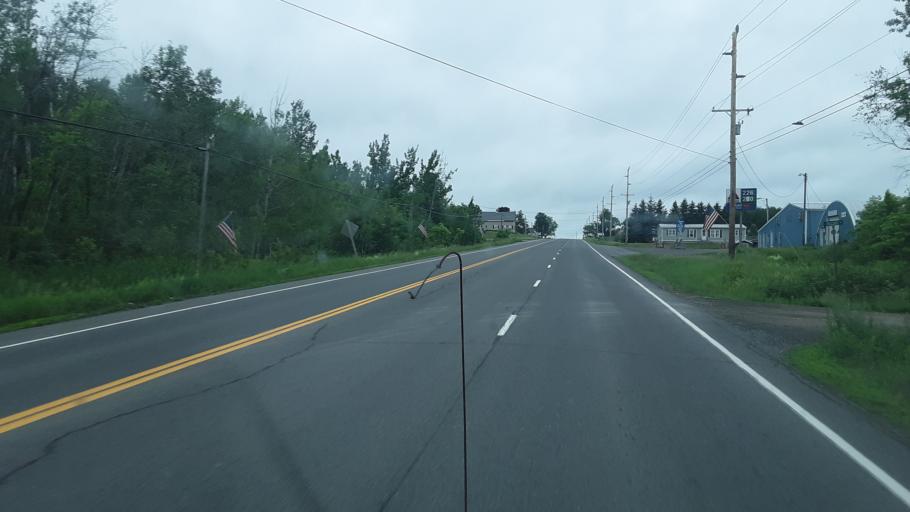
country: US
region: Maine
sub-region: Penobscot County
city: Patten
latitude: 45.9877
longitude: -68.4496
